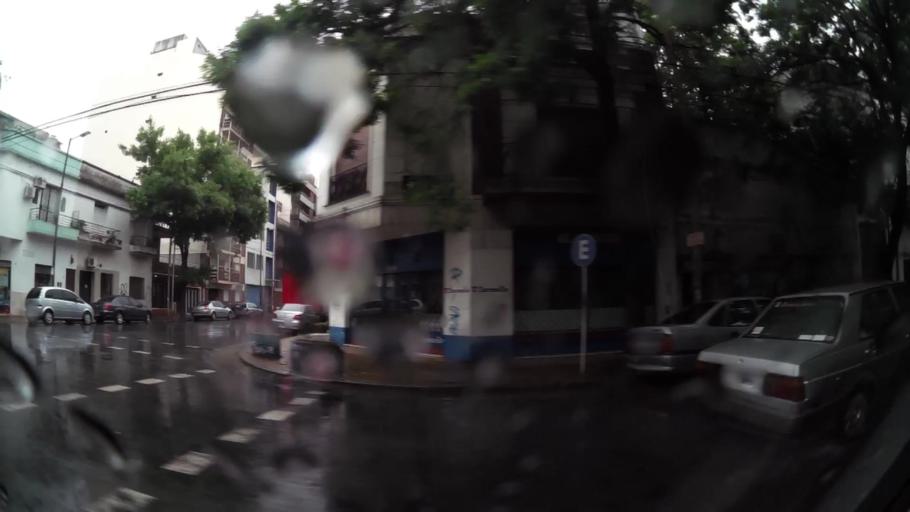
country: AR
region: Buenos Aires F.D.
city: Buenos Aires
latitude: -34.6359
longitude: -58.3718
